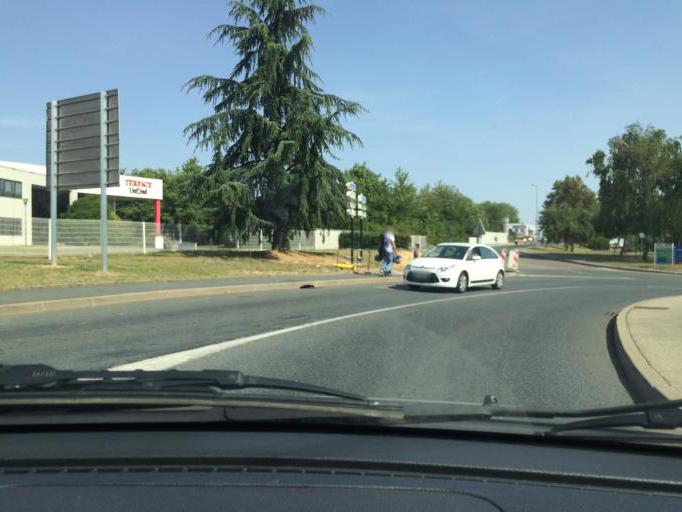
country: FR
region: Rhone-Alpes
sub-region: Departement du Rhone
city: Dardilly
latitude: 45.8055
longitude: 4.7714
